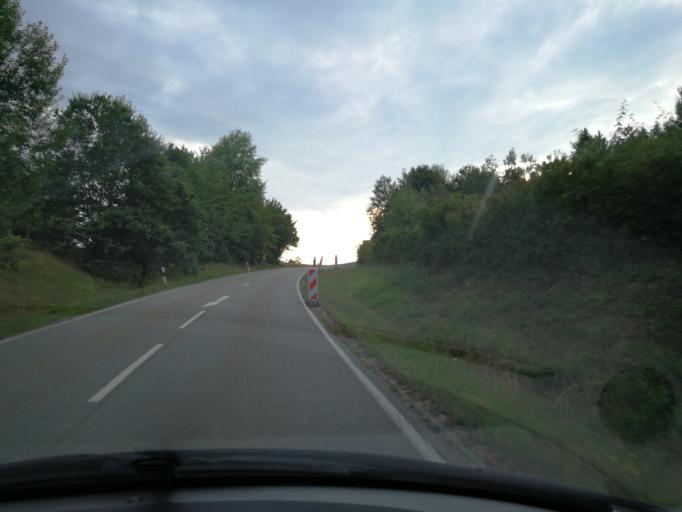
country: DE
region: Bavaria
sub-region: Lower Bavaria
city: Rattiszell
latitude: 49.0315
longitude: 12.6543
